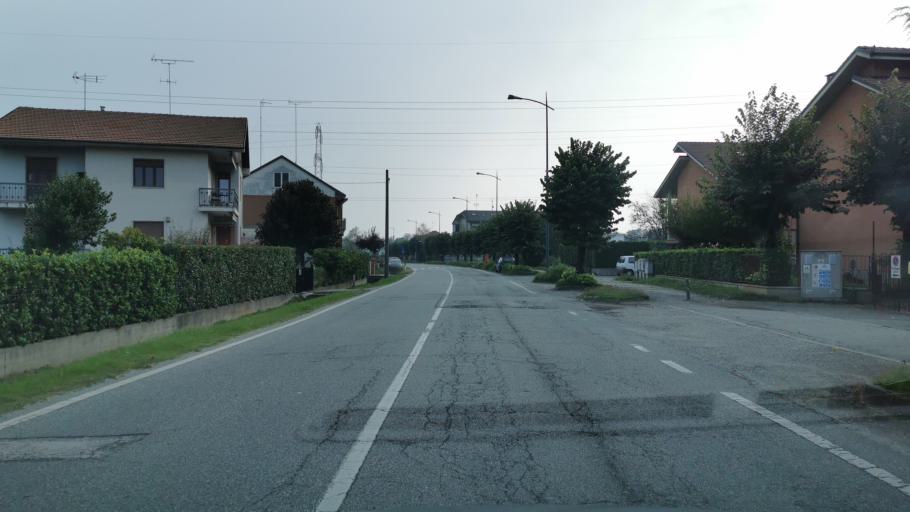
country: IT
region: Piedmont
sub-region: Provincia di Torino
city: Lombardore
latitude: 45.2331
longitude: 7.7415
